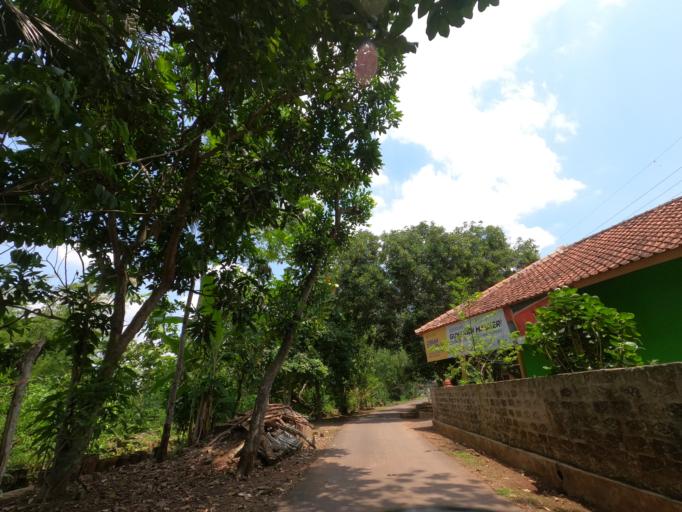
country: ID
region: West Java
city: Pamanukan
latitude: -6.5052
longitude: 107.7723
